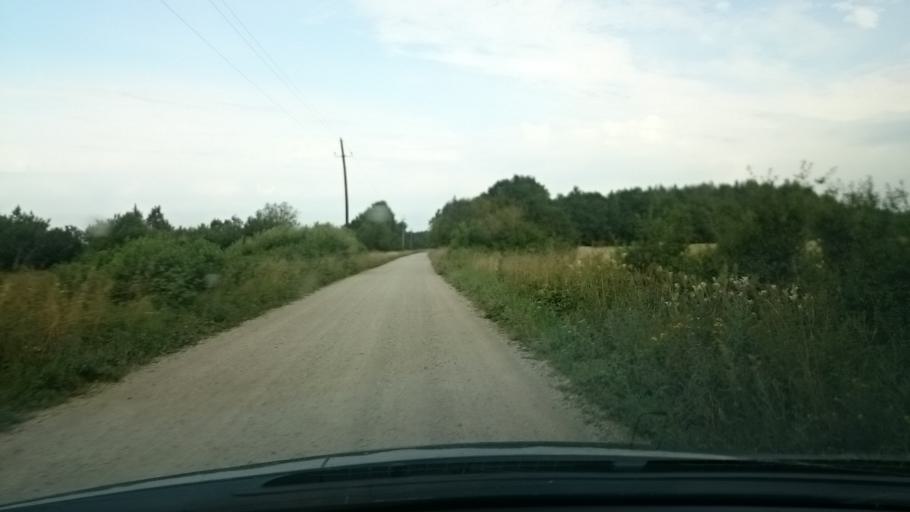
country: EE
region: Saare
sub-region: Kuressaare linn
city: Kuressaare
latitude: 58.3203
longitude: 21.9961
